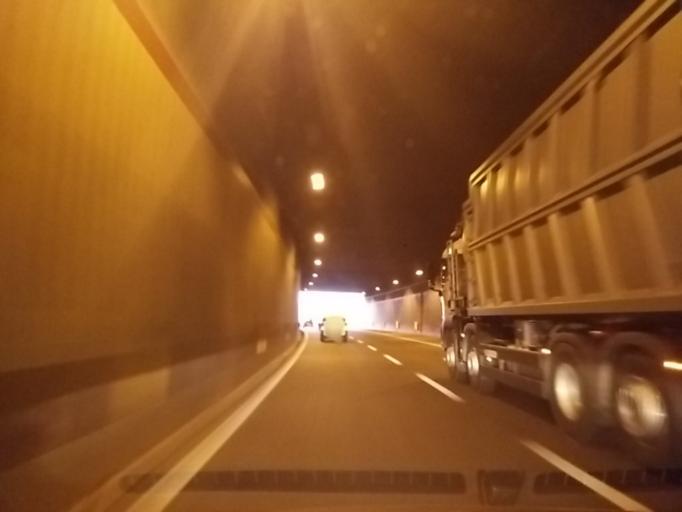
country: IT
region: Lombardy
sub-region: Provincia di Monza e Brianza
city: Muggio
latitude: 45.5731
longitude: 9.2246
